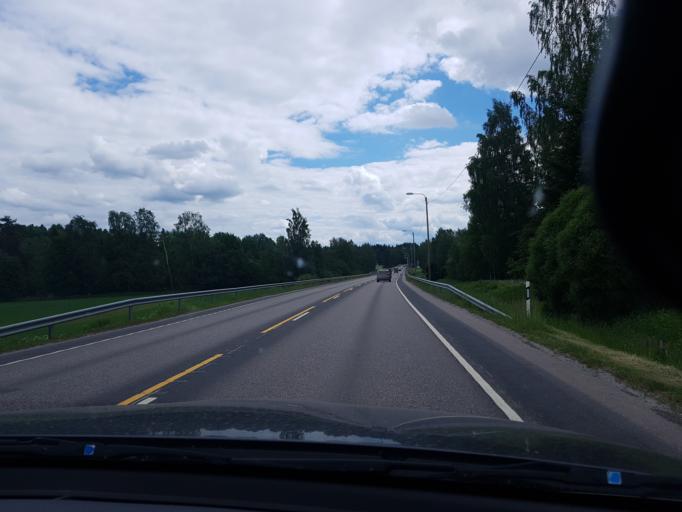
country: FI
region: Pirkanmaa
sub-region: Tampere
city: Paelkaene
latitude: 61.3381
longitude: 24.2778
